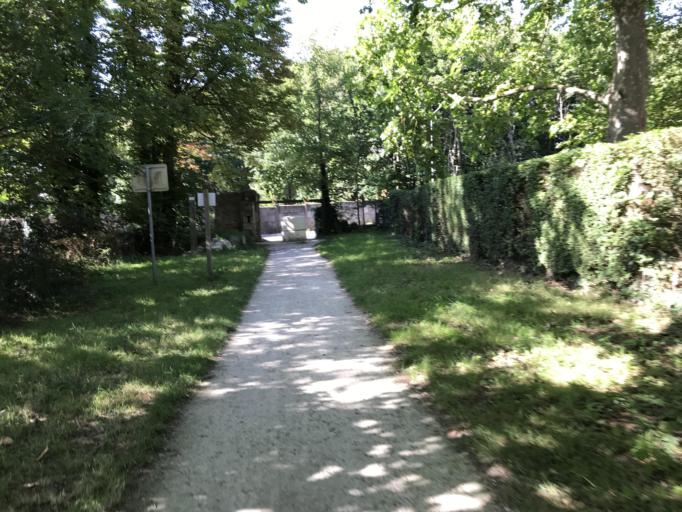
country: FR
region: Ile-de-France
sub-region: Departement de l'Essonne
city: Longpont-sur-Orge
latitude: 48.6443
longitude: 2.3011
